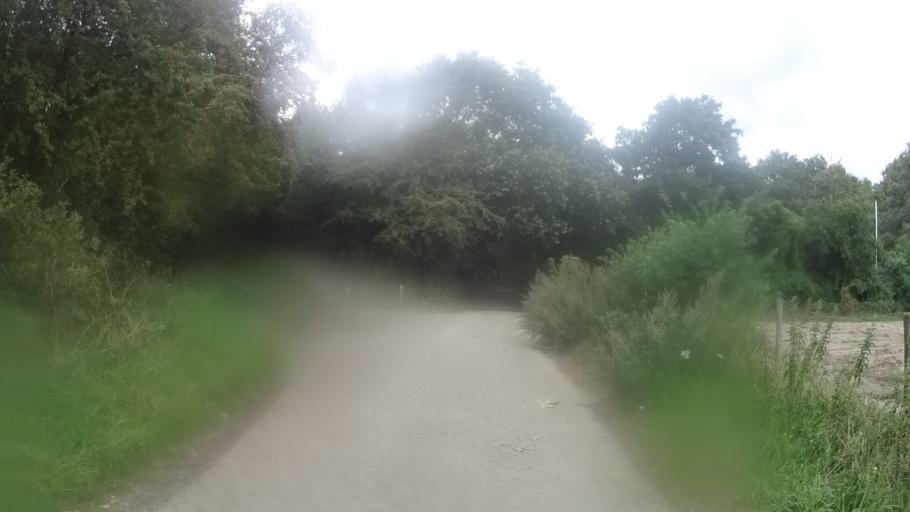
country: NL
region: North Holland
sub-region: Gemeente Castricum
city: Castricum
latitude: 52.5505
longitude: 4.6475
